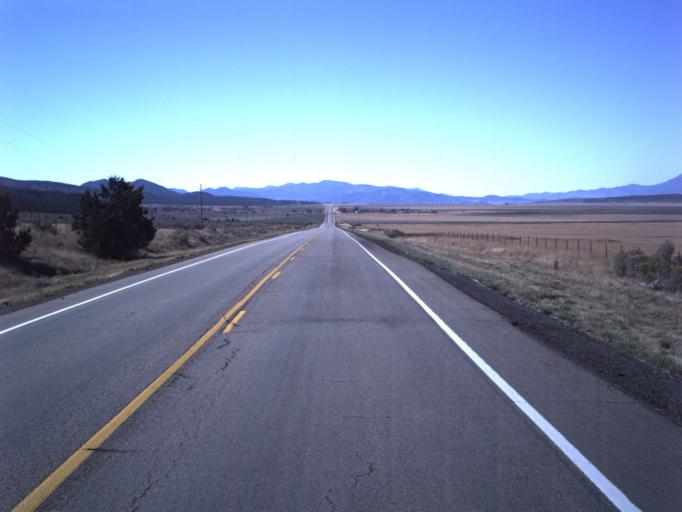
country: US
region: Utah
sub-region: Juab County
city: Nephi
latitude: 39.5012
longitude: -111.8755
